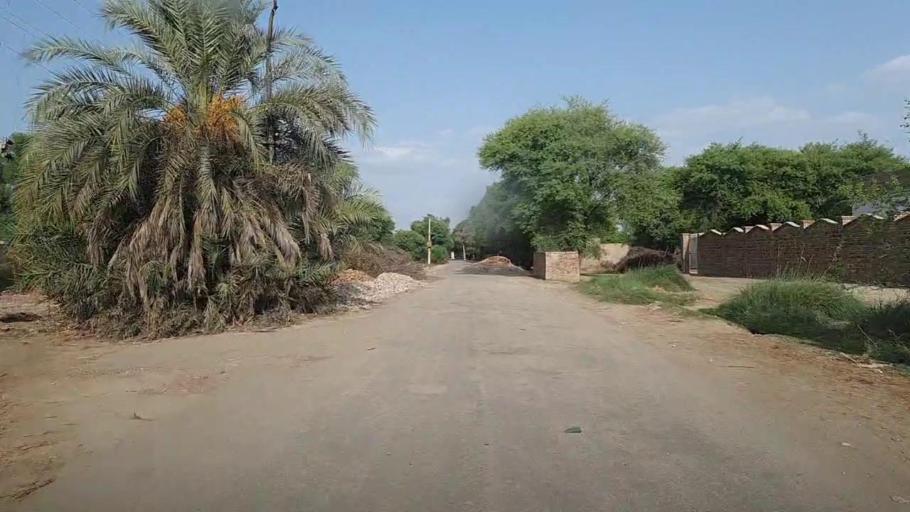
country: PK
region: Sindh
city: Khairpur
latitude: 28.0743
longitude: 69.8241
